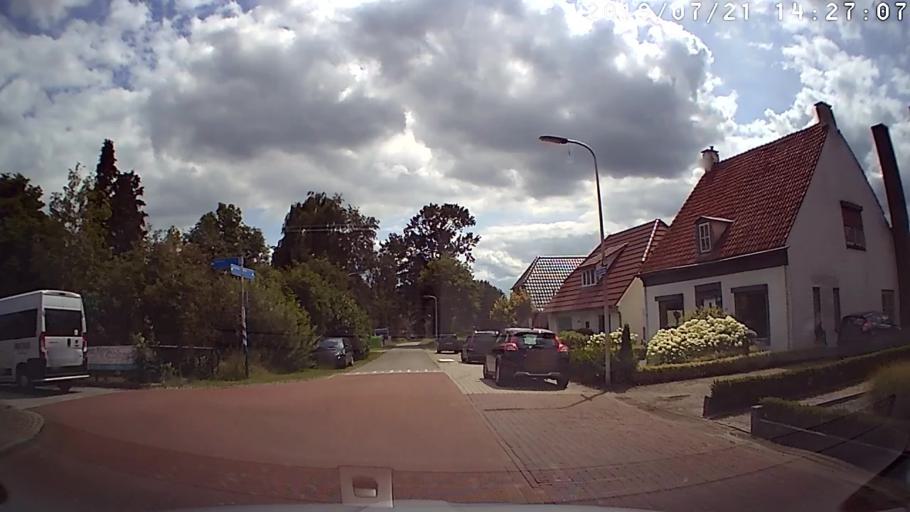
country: NL
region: Overijssel
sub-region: Gemeente Raalte
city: Heino
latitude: 52.4354
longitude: 6.1940
